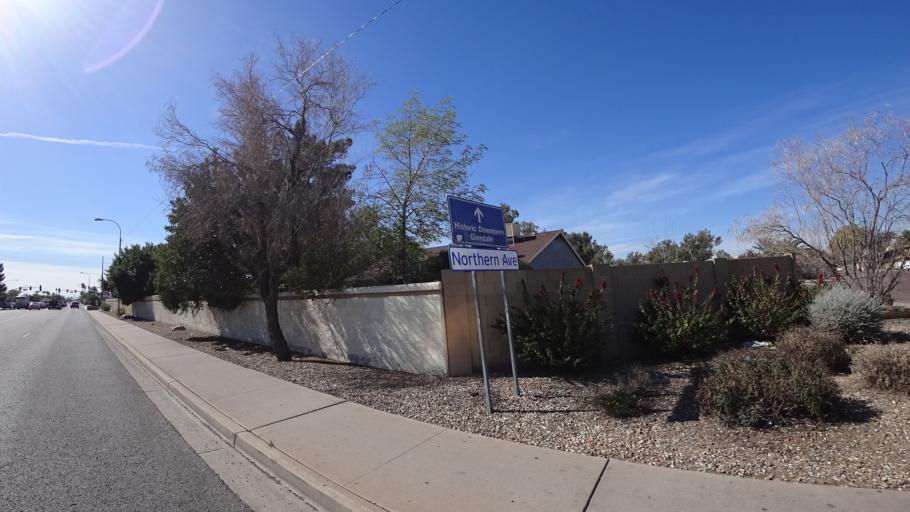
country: US
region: Arizona
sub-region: Maricopa County
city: Glendale
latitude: 33.5549
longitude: -112.1863
